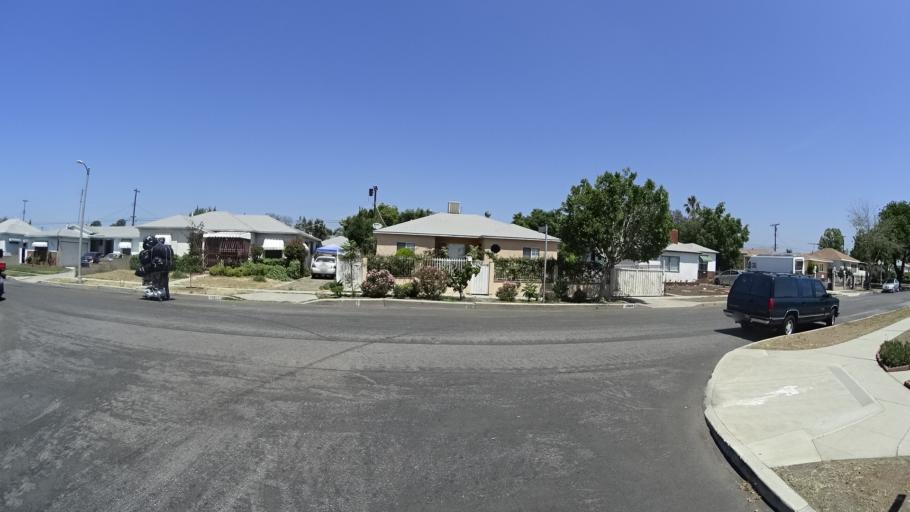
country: US
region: California
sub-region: Los Angeles County
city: San Fernando
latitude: 34.2341
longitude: -118.4339
